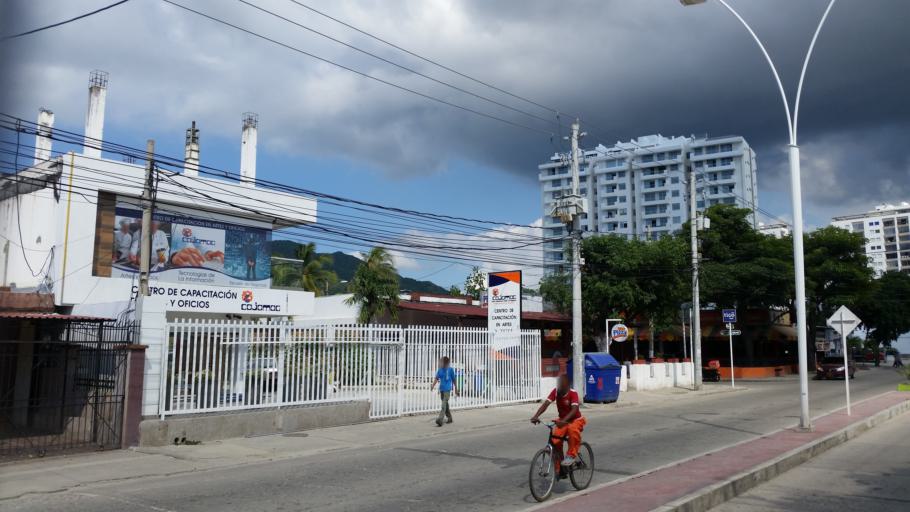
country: CO
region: Magdalena
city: Santa Marta
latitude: 11.2412
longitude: -74.1933
